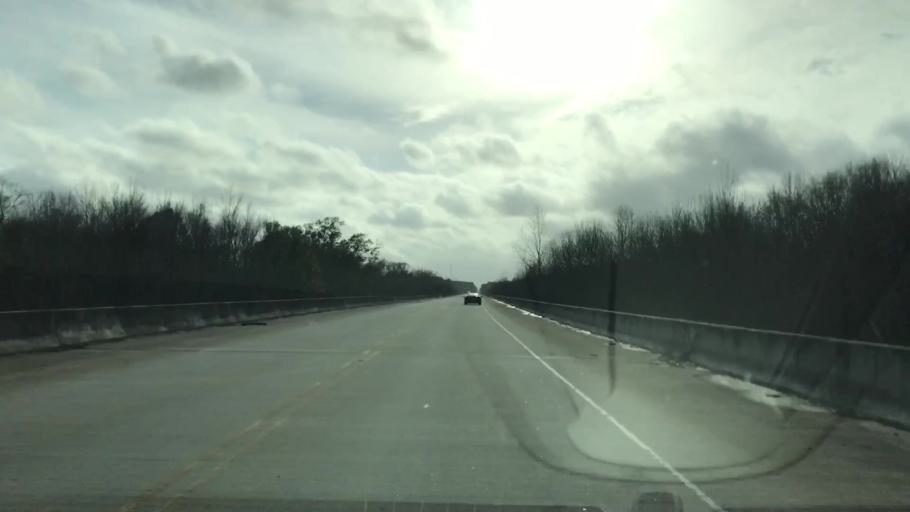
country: US
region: South Carolina
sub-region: Williamsburg County
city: Andrews
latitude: 33.3104
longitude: -79.6733
